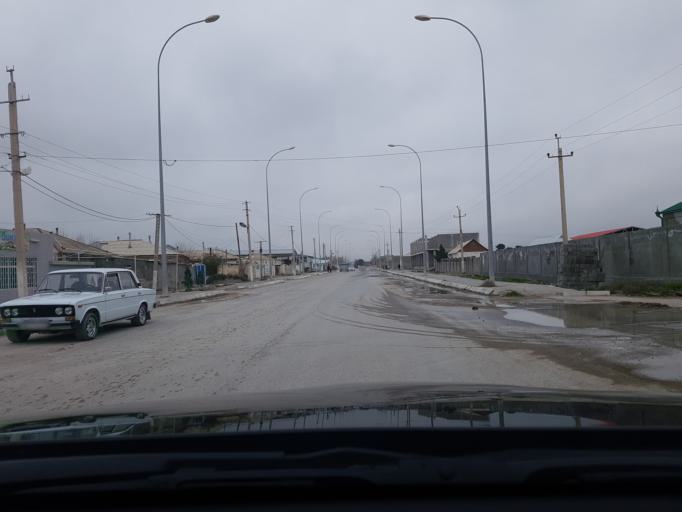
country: TM
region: Ahal
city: Abadan
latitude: 38.1541
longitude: 57.9566
